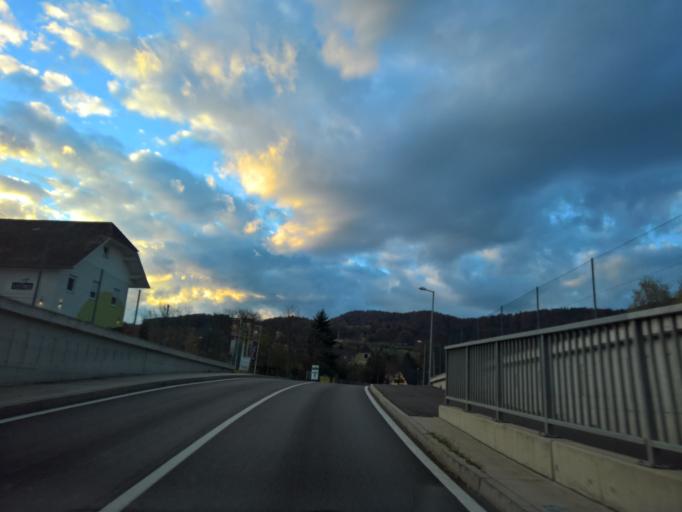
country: AT
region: Styria
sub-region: Politischer Bezirk Leibnitz
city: Stocking
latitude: 46.8614
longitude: 15.5291
